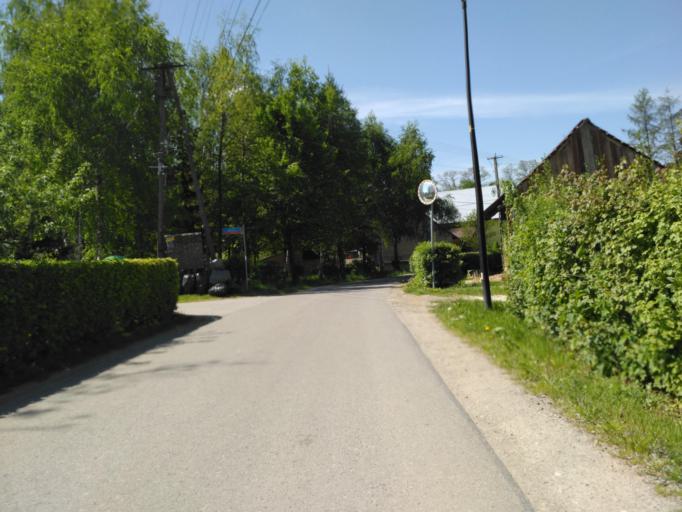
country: PL
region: Subcarpathian Voivodeship
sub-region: Powiat krosnienski
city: Miejsce Piastowe
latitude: 49.6157
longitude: 21.7614
